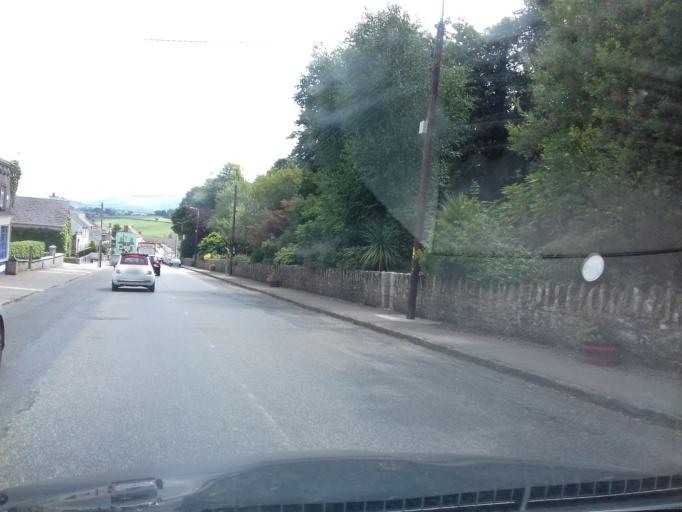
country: IE
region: Leinster
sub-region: Kilkenny
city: Graiguenamanagh
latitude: 52.6009
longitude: -6.9265
